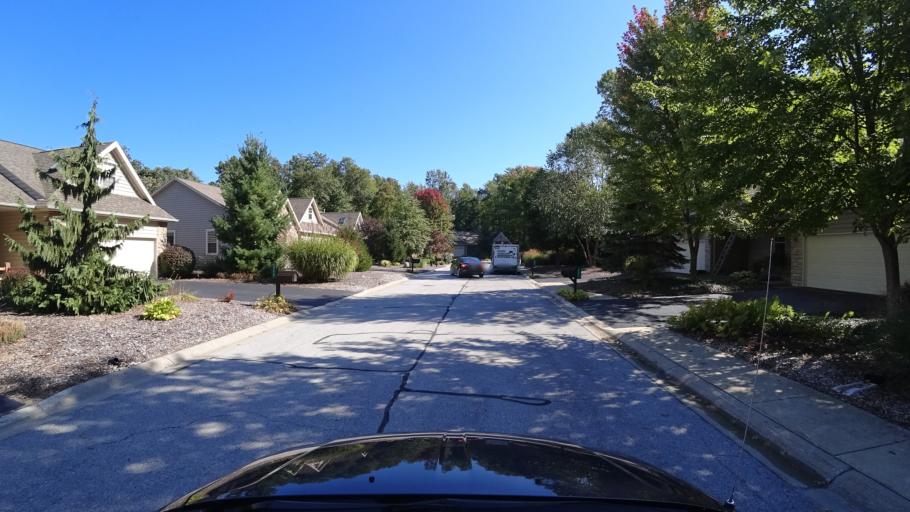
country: US
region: Indiana
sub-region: LaPorte County
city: Trail Creek
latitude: 41.6966
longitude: -86.8763
